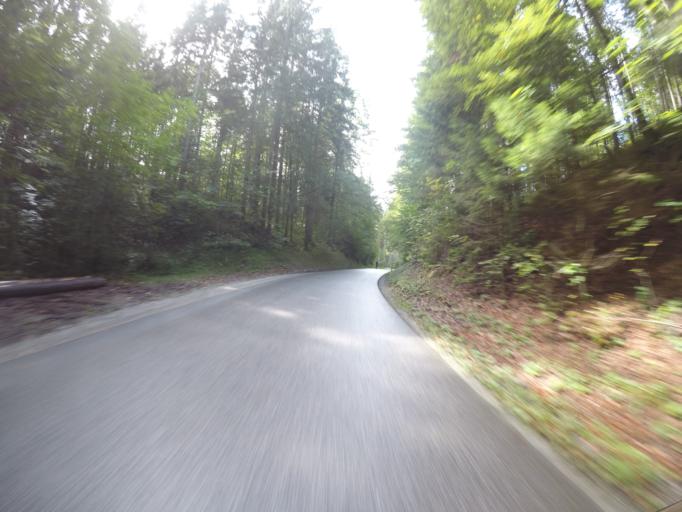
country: DE
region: Bavaria
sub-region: Upper Bavaria
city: Wallgau
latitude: 47.5290
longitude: 11.3019
